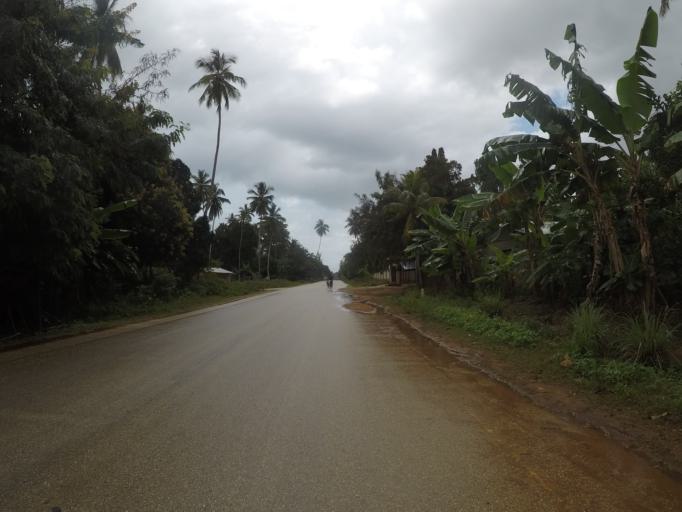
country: TZ
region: Zanzibar North
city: Mkokotoni
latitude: -5.9764
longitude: 39.1962
